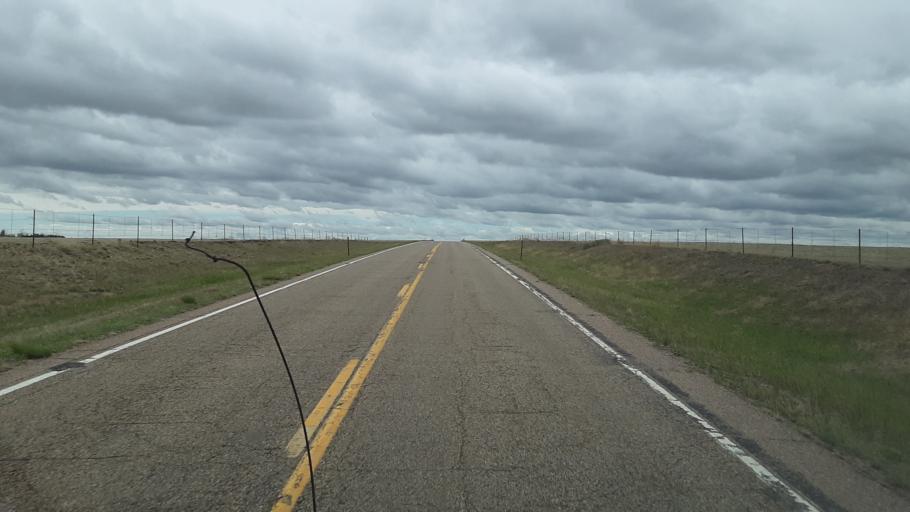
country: US
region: Colorado
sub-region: El Paso County
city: Ellicott
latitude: 38.8394
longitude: -103.9103
